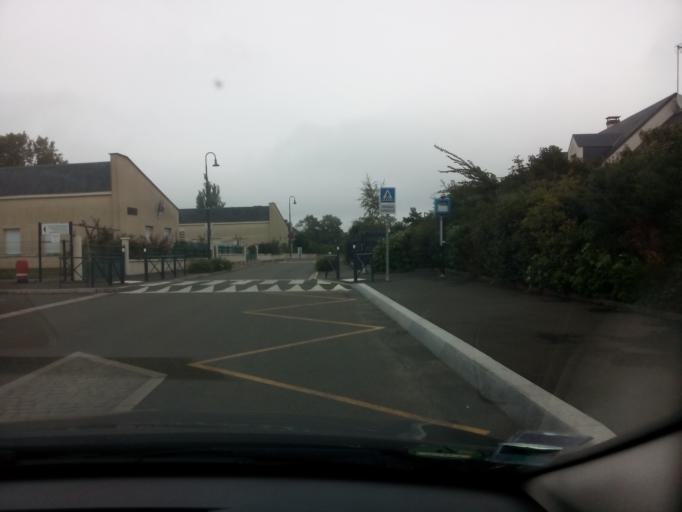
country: FR
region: Pays de la Loire
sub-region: Departement de Maine-et-Loire
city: Soulaire-et-Bourg
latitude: 47.5773
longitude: -0.5543
